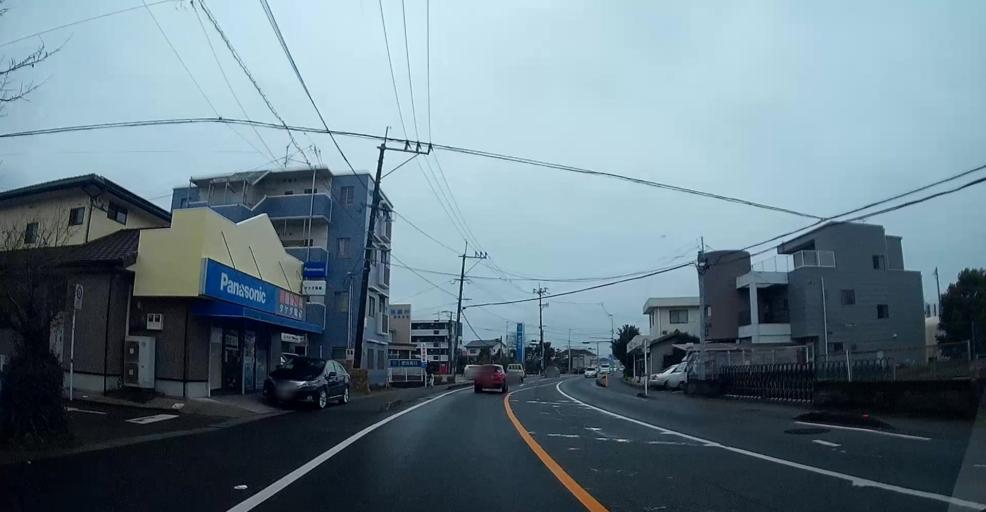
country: JP
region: Kumamoto
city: Kumamoto
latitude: 32.7432
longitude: 130.7405
